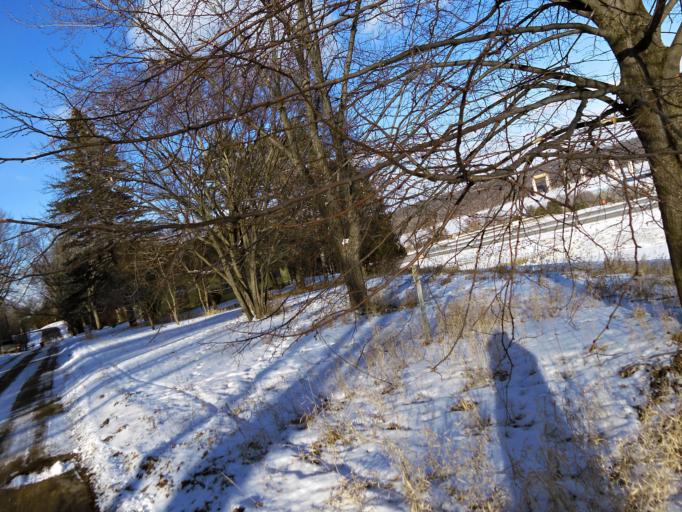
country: US
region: Minnesota
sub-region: Washington County
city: Oak Park Heights
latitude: 45.0382
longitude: -92.7960
